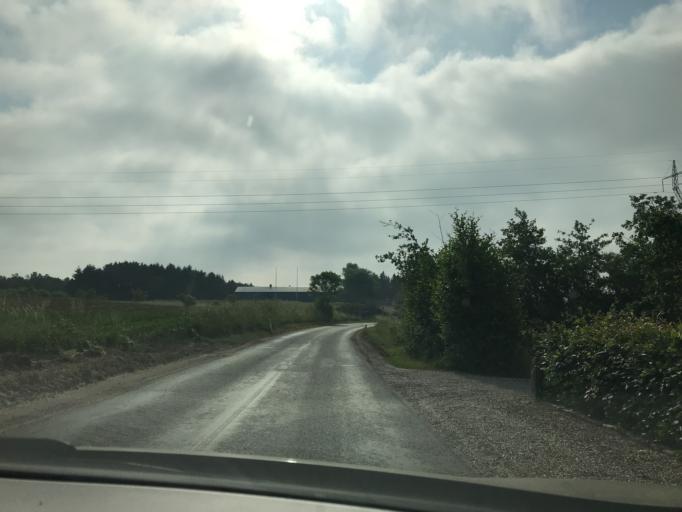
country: DK
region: South Denmark
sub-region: Odense Kommune
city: Bellinge
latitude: 55.3746
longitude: 10.2911
